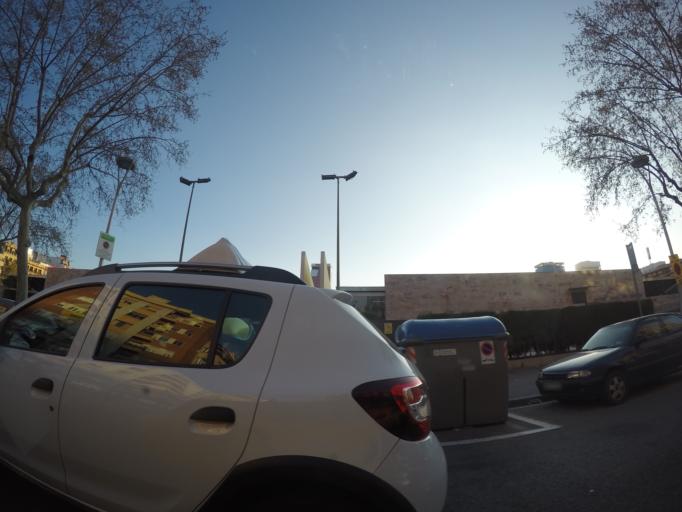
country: ES
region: Catalonia
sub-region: Provincia de Barcelona
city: Sants-Montjuic
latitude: 41.3790
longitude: 2.1492
